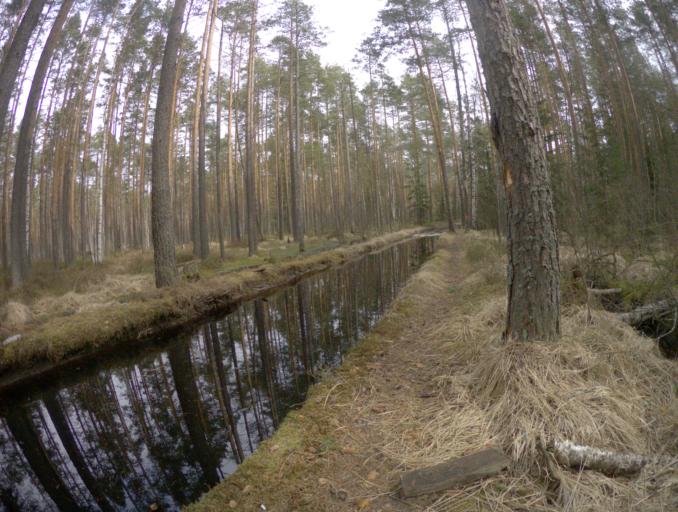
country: RU
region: Vladimir
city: Raduzhnyy
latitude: 55.9478
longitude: 40.2804
